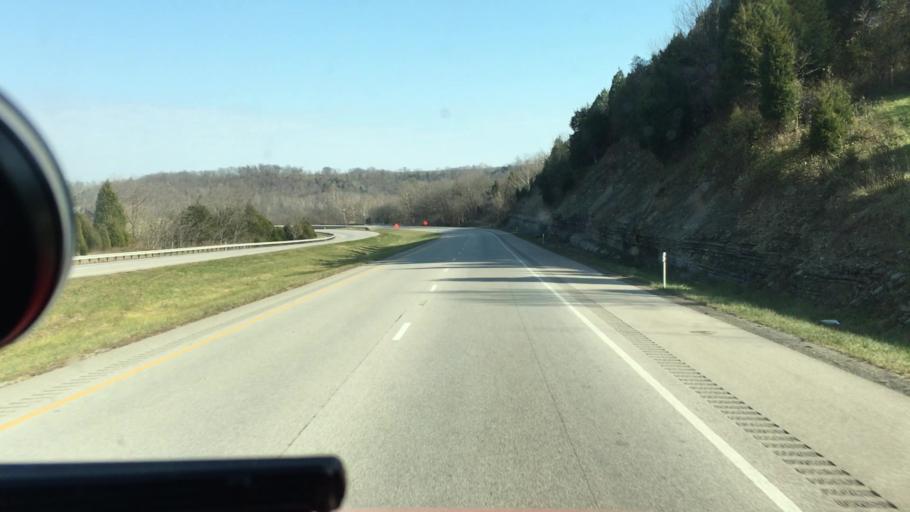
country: US
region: Kentucky
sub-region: Bath County
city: Owingsville
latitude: 38.1109
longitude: -83.8108
